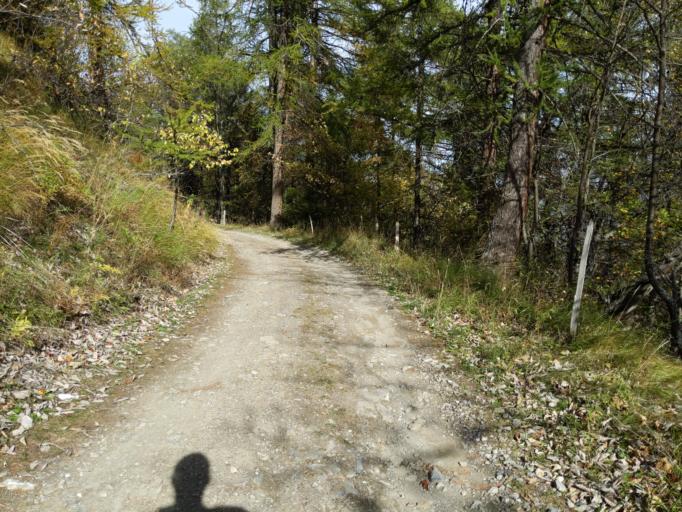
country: FR
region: Rhone-Alpes
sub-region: Departement de la Savoie
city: Valloire
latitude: 45.1936
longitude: 6.4282
